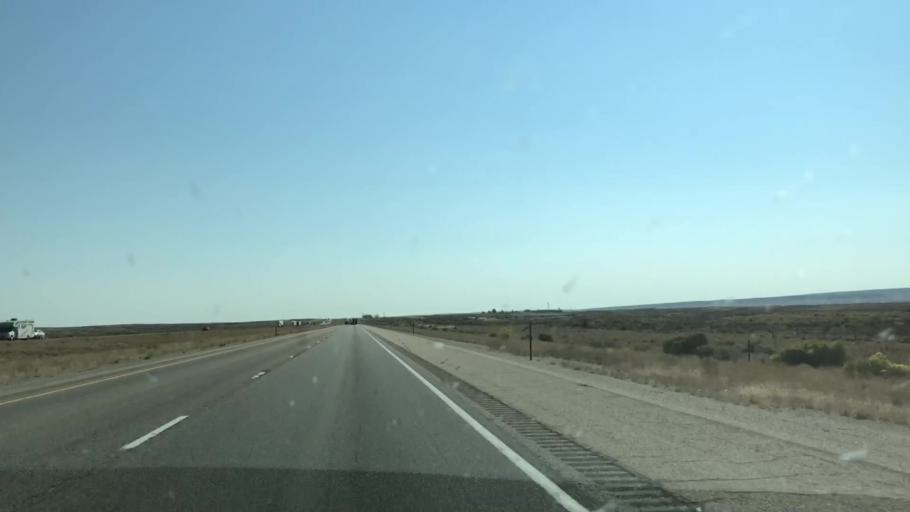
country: US
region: Wyoming
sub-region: Sweetwater County
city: Rock Springs
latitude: 41.6366
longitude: -108.4351
